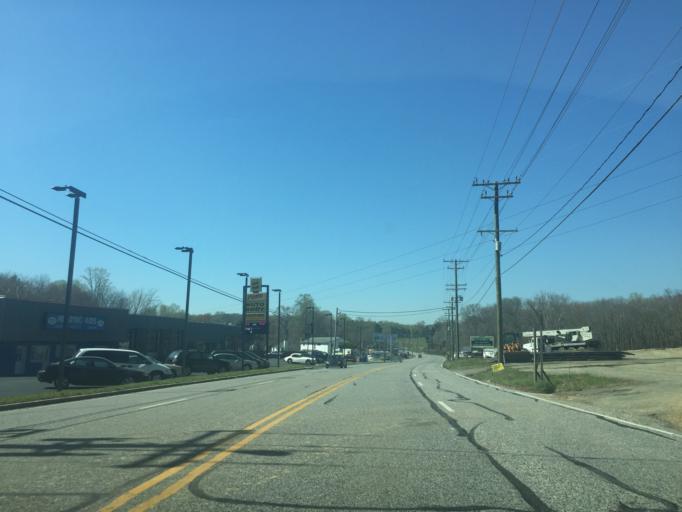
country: US
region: Maryland
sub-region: Harford County
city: Pleasant Hills
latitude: 39.4868
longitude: -76.3990
